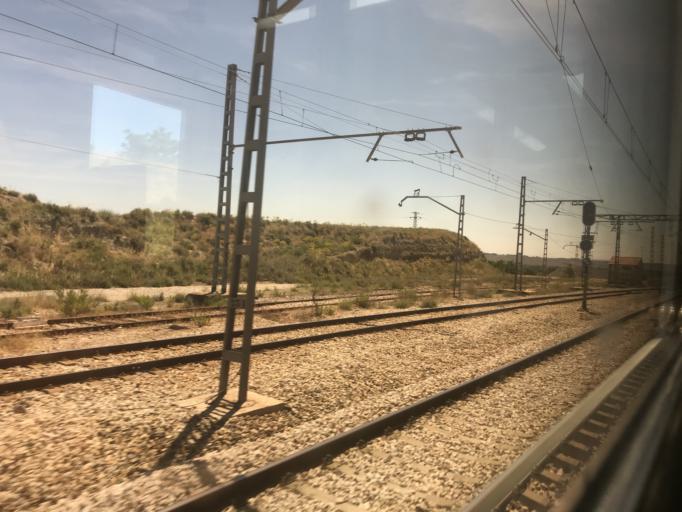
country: ES
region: Madrid
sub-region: Provincia de Madrid
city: Ciempozuelos
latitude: 40.1575
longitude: -3.6093
